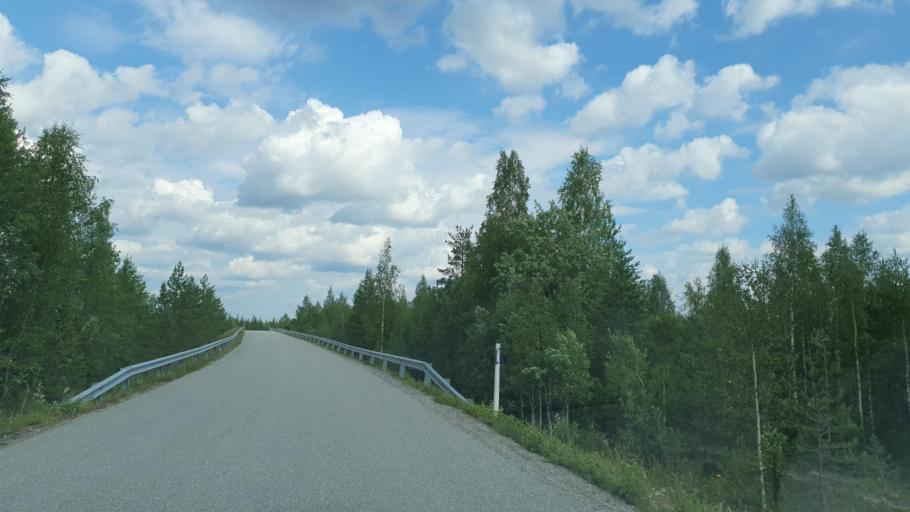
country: FI
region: Kainuu
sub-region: Kehys-Kainuu
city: Kuhmo
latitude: 64.4911
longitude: 29.5965
